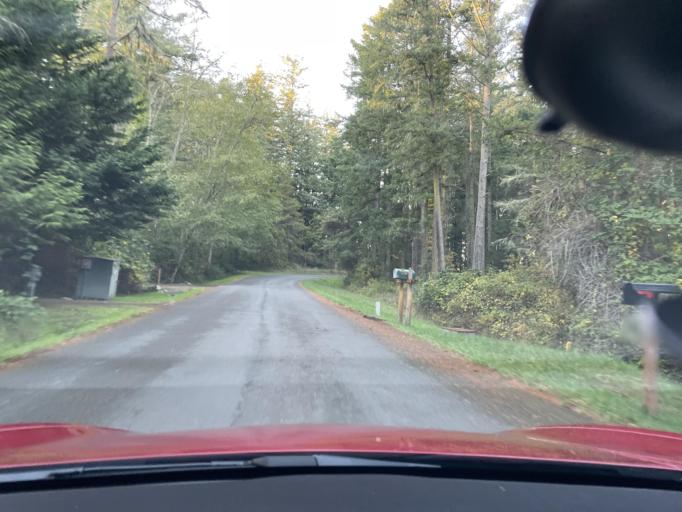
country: US
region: Washington
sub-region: San Juan County
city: Friday Harbor
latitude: 48.6073
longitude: -123.1461
